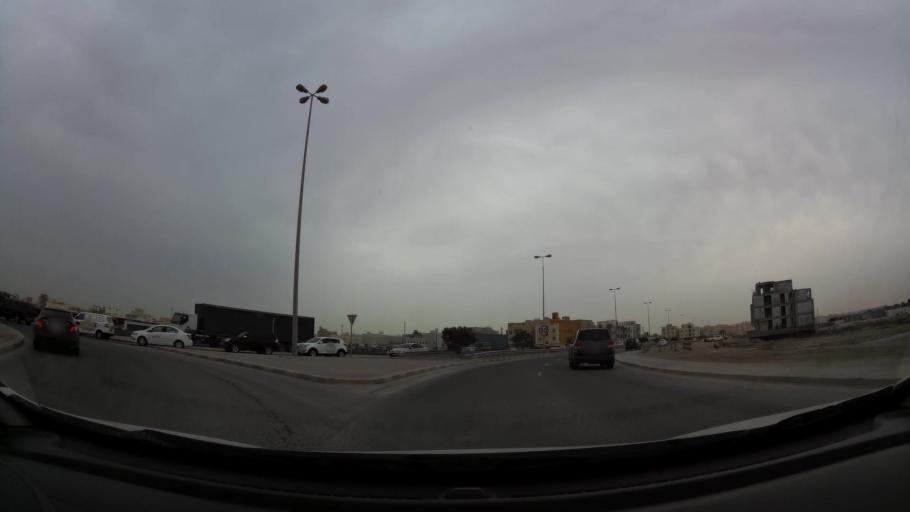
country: BH
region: Northern
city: Madinat `Isa
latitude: 26.1831
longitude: 50.5199
